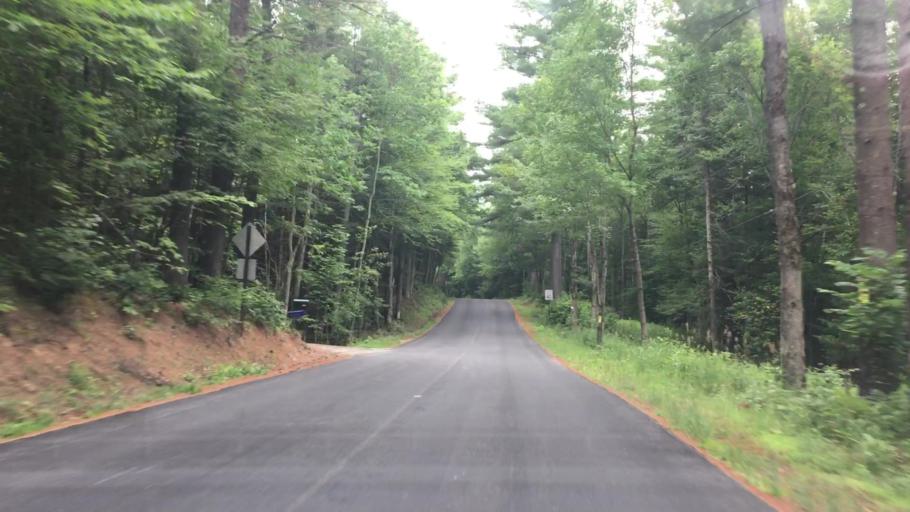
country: US
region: New York
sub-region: Essex County
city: Keeseville
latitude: 44.4261
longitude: -73.6315
